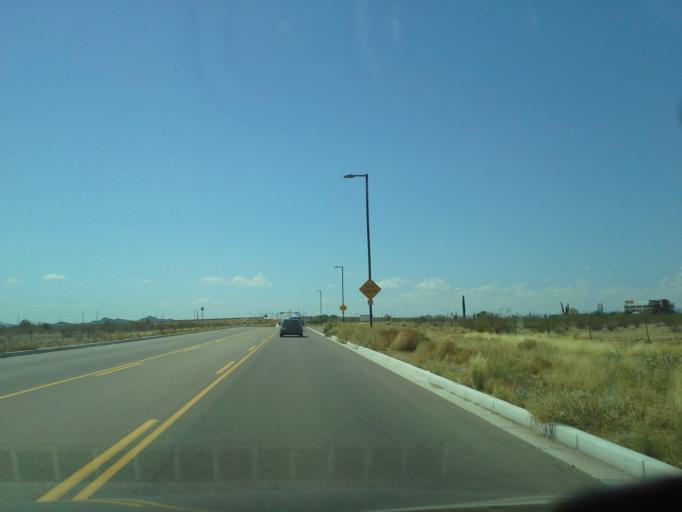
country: US
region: Arizona
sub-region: Maricopa County
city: Anthem
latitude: 33.7839
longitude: -112.1222
